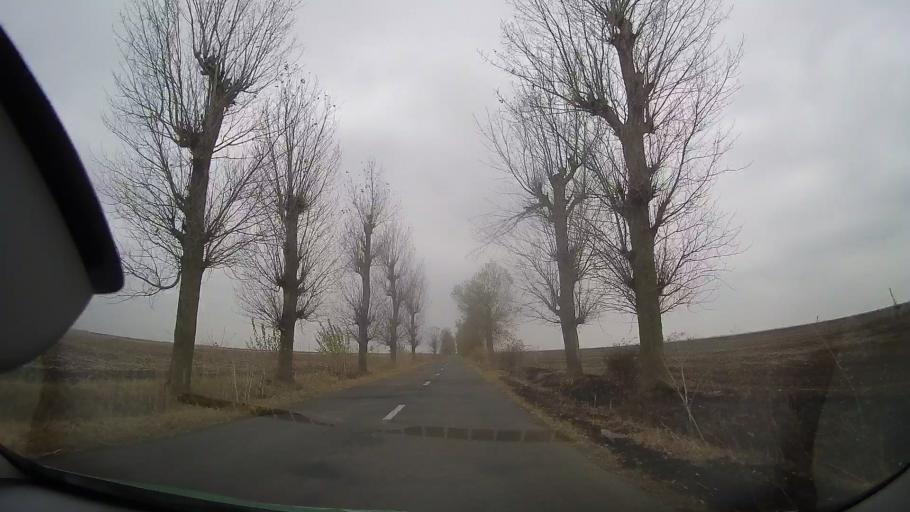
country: RO
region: Ialomita
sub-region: Comuna Grindu
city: Grindu
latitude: 44.7707
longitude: 26.8847
